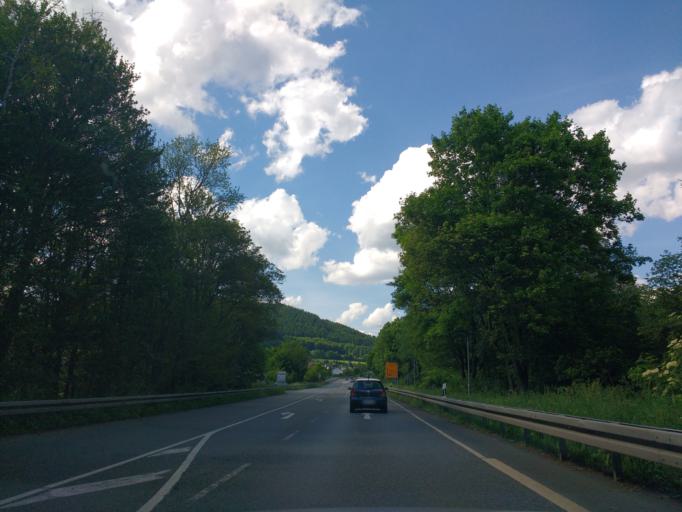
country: DE
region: Hesse
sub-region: Regierungsbezirk Giessen
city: Breidenbach
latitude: 50.9178
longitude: 8.4686
